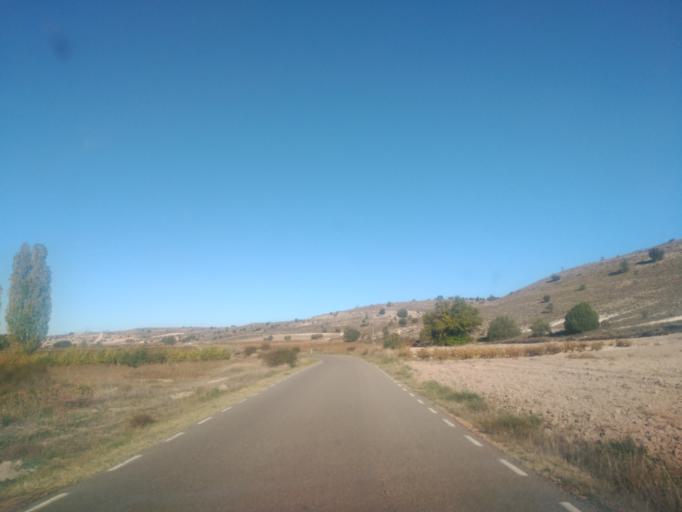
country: ES
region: Castille and Leon
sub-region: Provincia de Burgos
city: Penaranda de Duero
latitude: 41.6850
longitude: -3.4348
